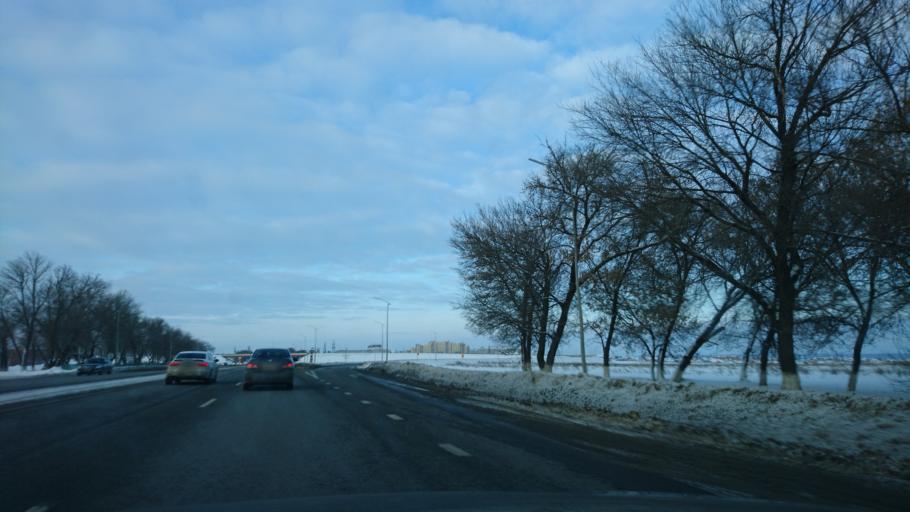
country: RU
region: Belgorod
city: Severnyy
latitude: 50.6638
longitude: 36.5623
